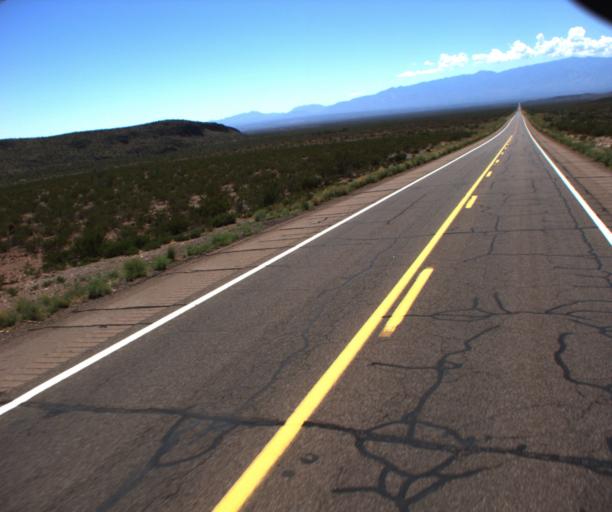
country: US
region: Arizona
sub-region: Greenlee County
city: Clifton
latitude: 32.8436
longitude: -109.4173
